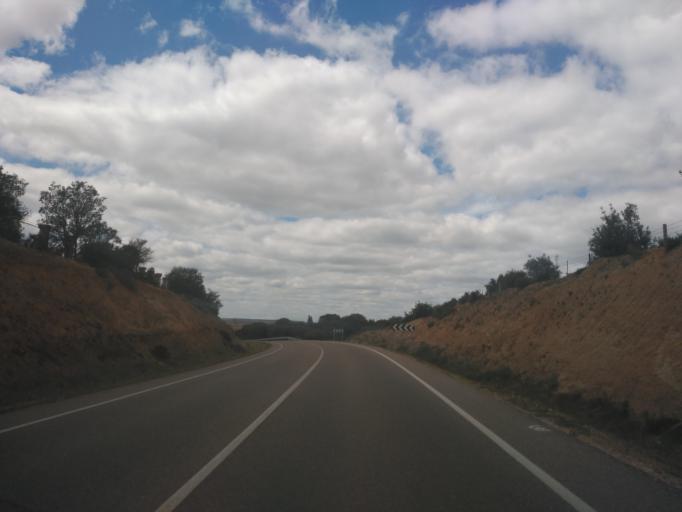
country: ES
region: Castille and Leon
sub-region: Provincia de Salamanca
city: Florida de Liebana
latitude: 41.0385
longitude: -5.7421
